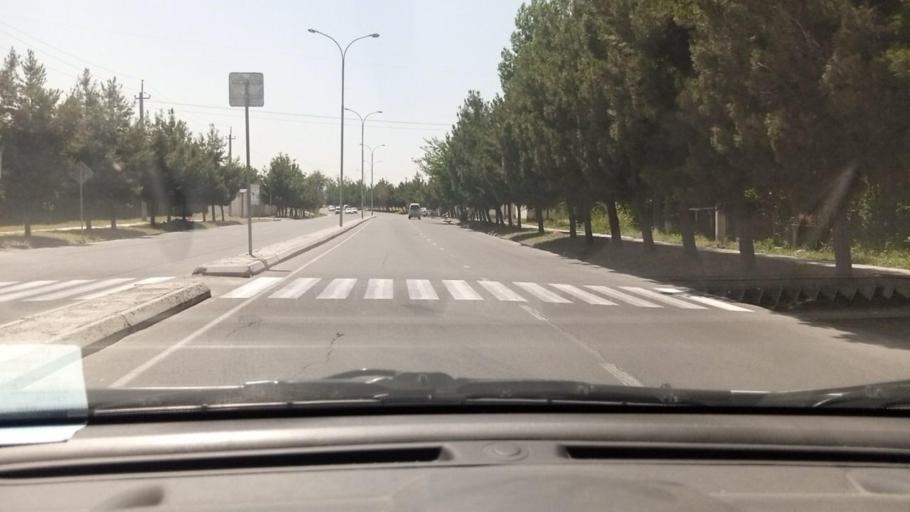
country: UZ
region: Toshkent
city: Urtaowul
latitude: 41.2228
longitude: 69.1769
